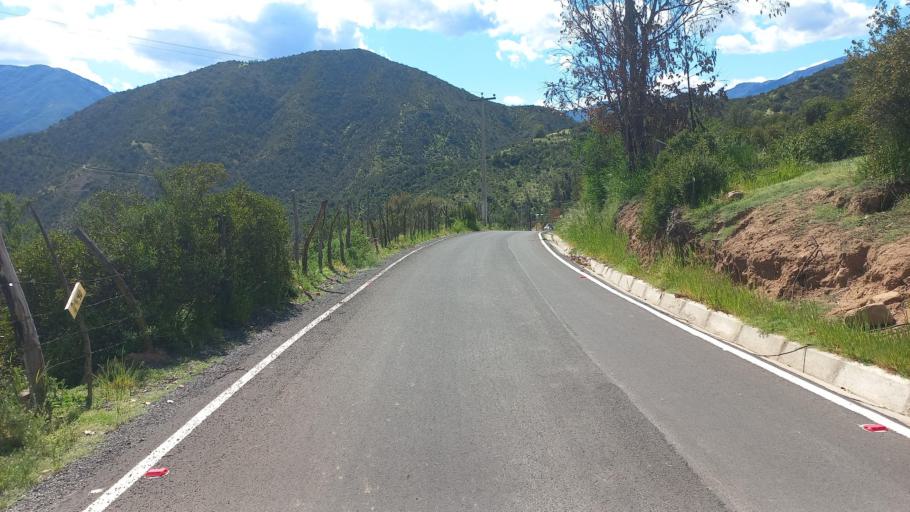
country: CL
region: Santiago Metropolitan
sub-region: Provincia de Chacabuco
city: Lampa
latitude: -33.1925
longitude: -71.0905
